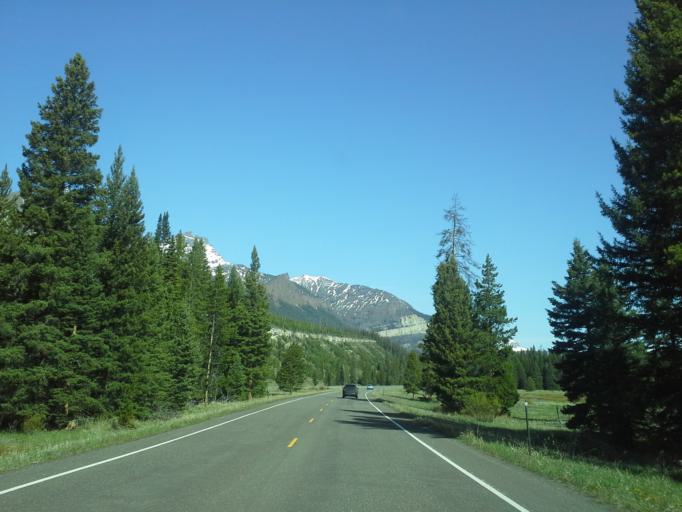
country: US
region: Montana
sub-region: Carbon County
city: Red Lodge
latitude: 44.9614
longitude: -109.8190
